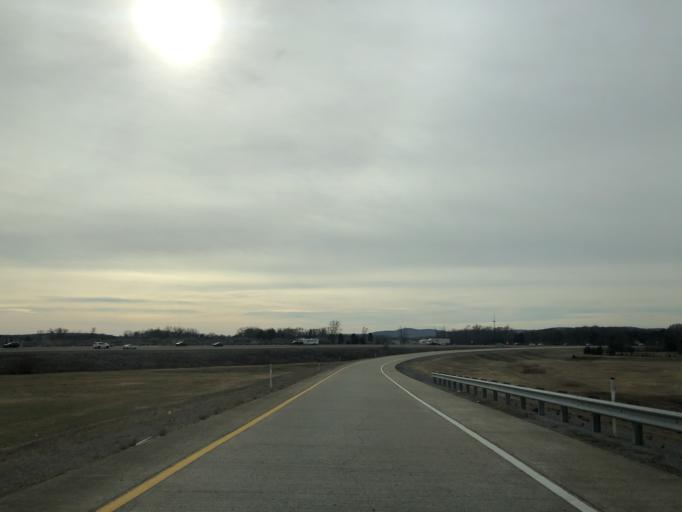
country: US
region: Tennessee
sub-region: Rutherford County
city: Smyrna
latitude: 35.8677
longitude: -86.5131
